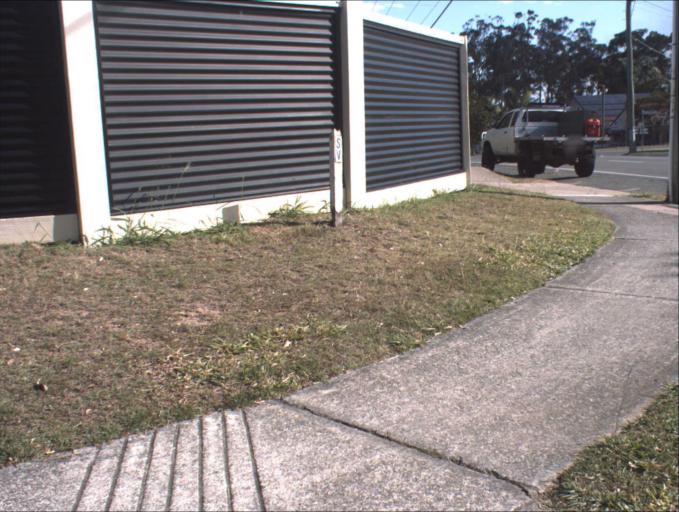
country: AU
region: Queensland
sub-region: Logan
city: Logan City
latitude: -27.6585
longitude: 153.0985
